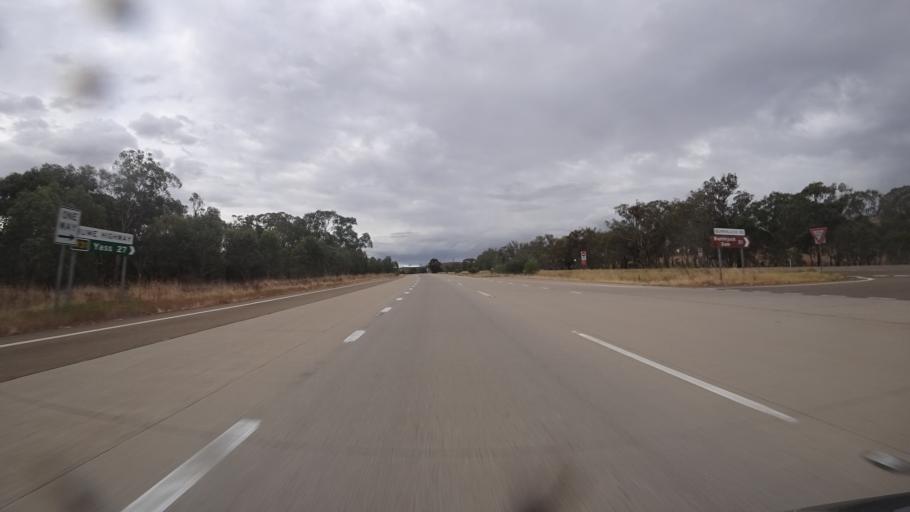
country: AU
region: New South Wales
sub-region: Yass Valley
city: Yass
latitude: -34.8101
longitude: 148.6886
